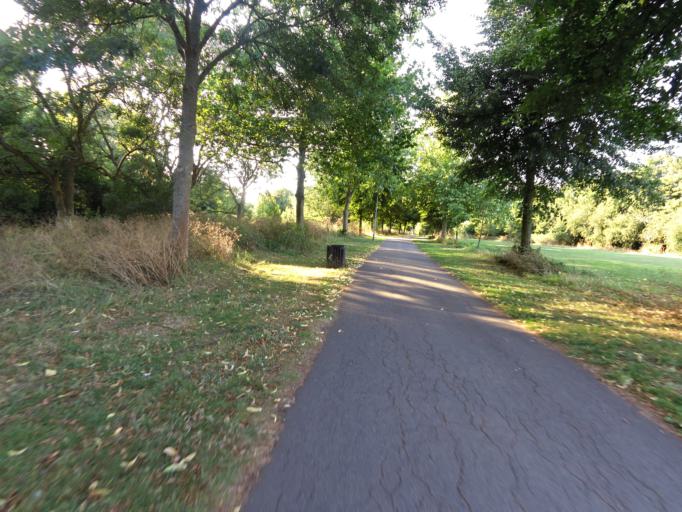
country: GB
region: England
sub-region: Essex
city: Chelmsford
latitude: 51.7350
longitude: 0.4569
